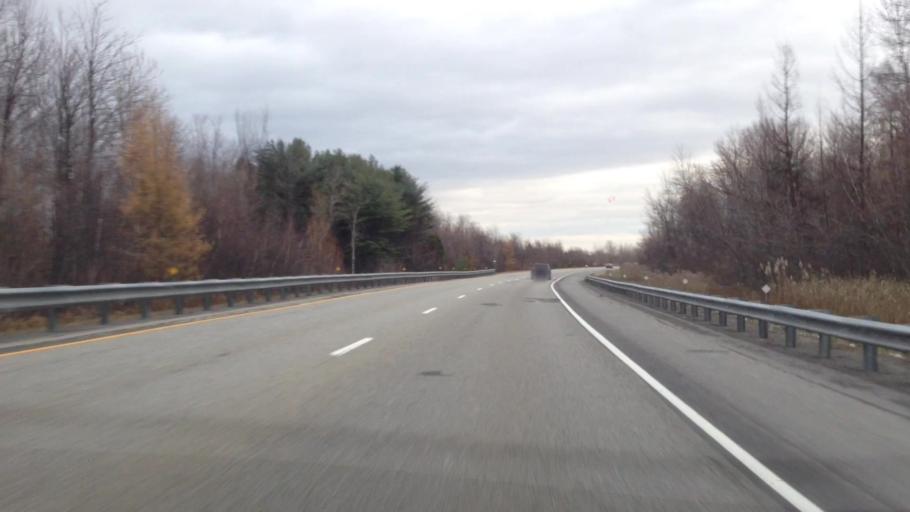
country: CA
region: Ontario
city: Casselman
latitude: 45.3159
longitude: -75.1613
